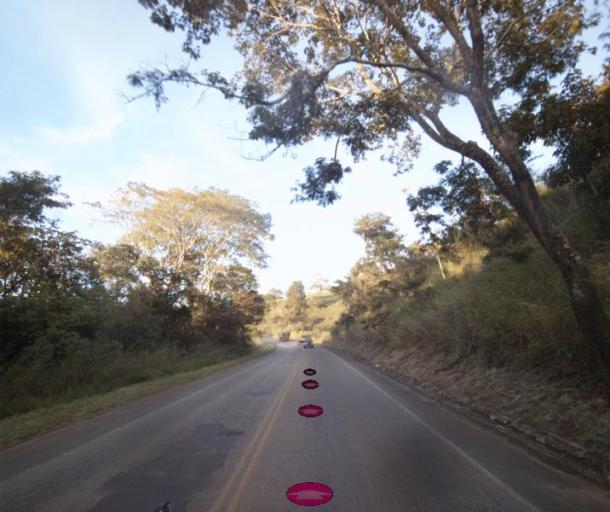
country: BR
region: Goias
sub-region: Abadiania
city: Abadiania
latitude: -16.1161
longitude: -48.8882
